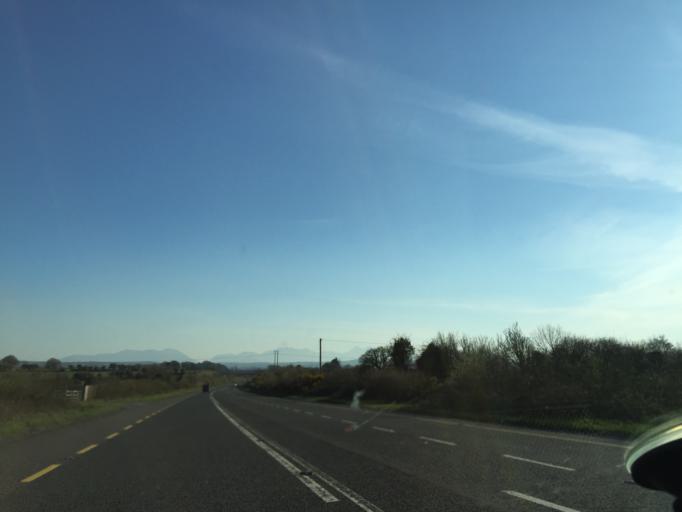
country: IE
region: Munster
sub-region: Ciarrai
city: Castleisland
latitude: 52.2100
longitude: -9.5662
